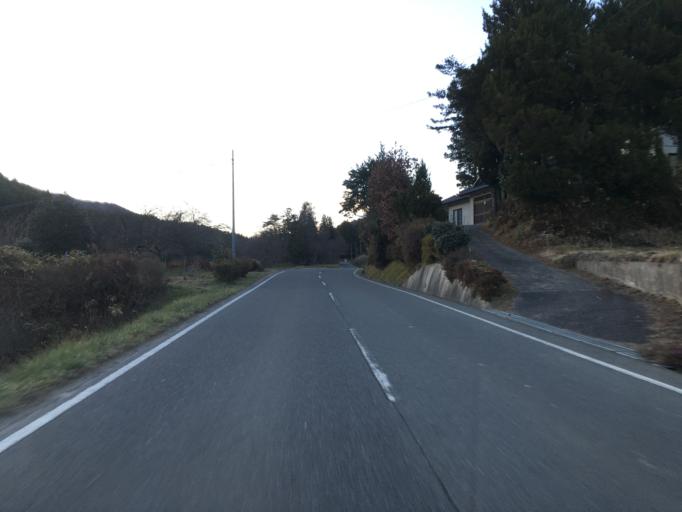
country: JP
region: Fukushima
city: Ishikawa
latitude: 37.2734
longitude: 140.5701
